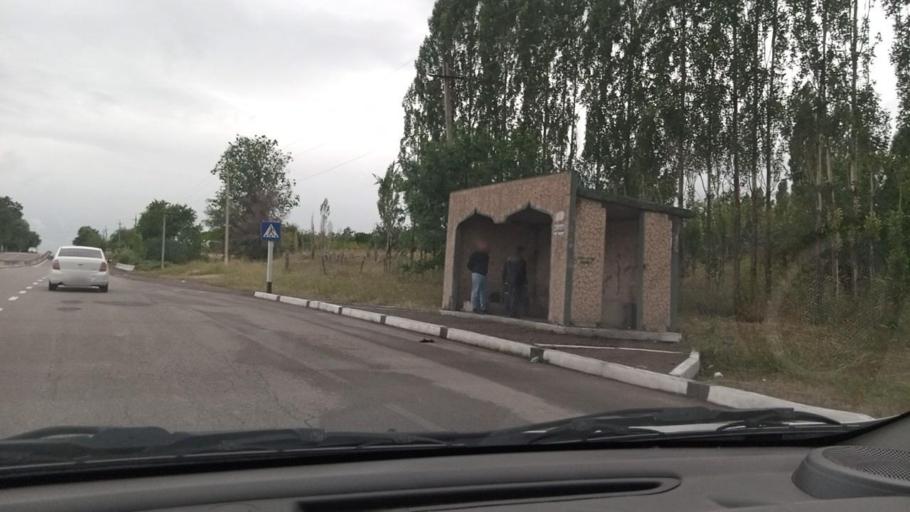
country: UZ
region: Toshkent
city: Angren
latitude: 40.9382
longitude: 69.8976
